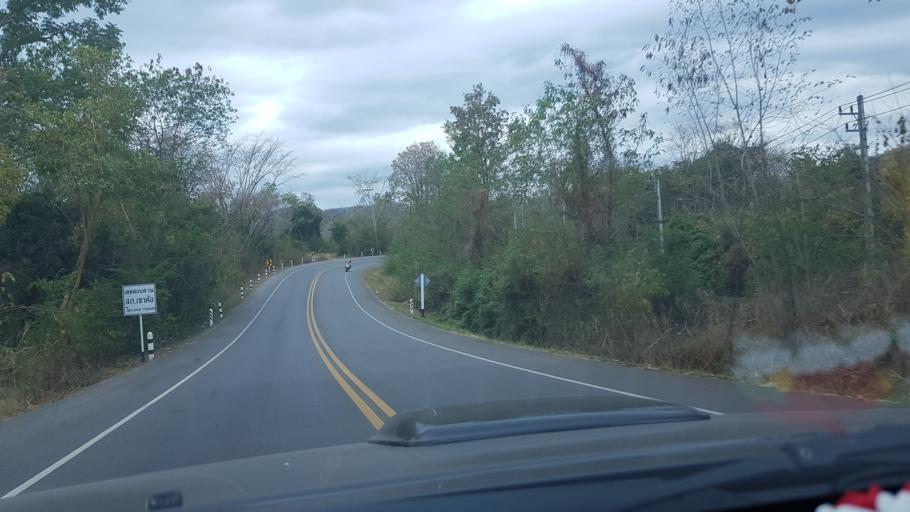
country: TH
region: Phetchabun
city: Phetchabun
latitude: 16.5332
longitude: 101.1103
